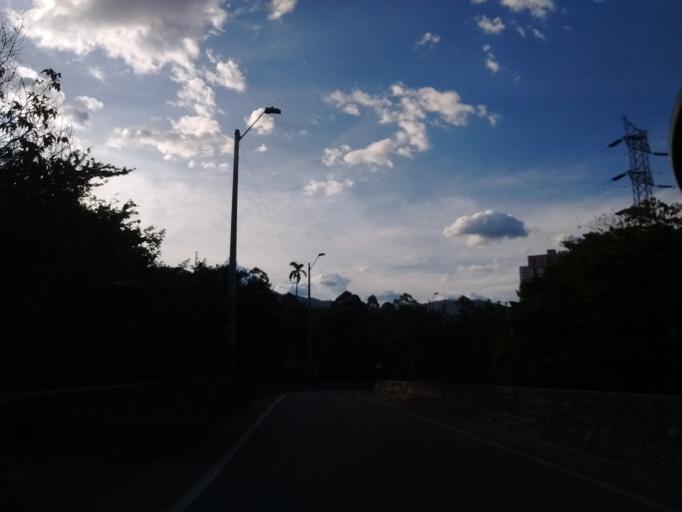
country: CO
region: Antioquia
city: Bello
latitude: 6.3099
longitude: -75.5581
